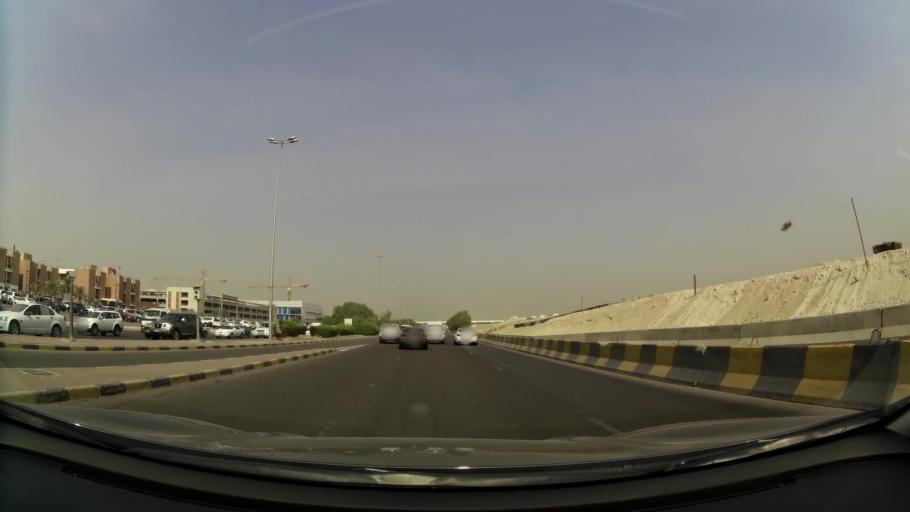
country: KW
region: Al Asimah
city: Ar Rabiyah
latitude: 29.2707
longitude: 47.9077
